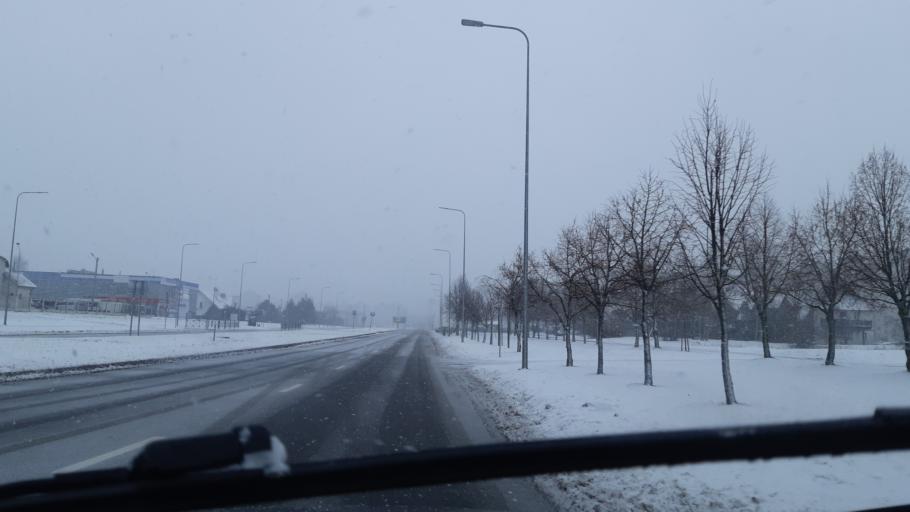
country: LT
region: Kauno apskritis
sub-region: Kaunas
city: Silainiai
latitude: 54.9264
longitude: 23.8764
